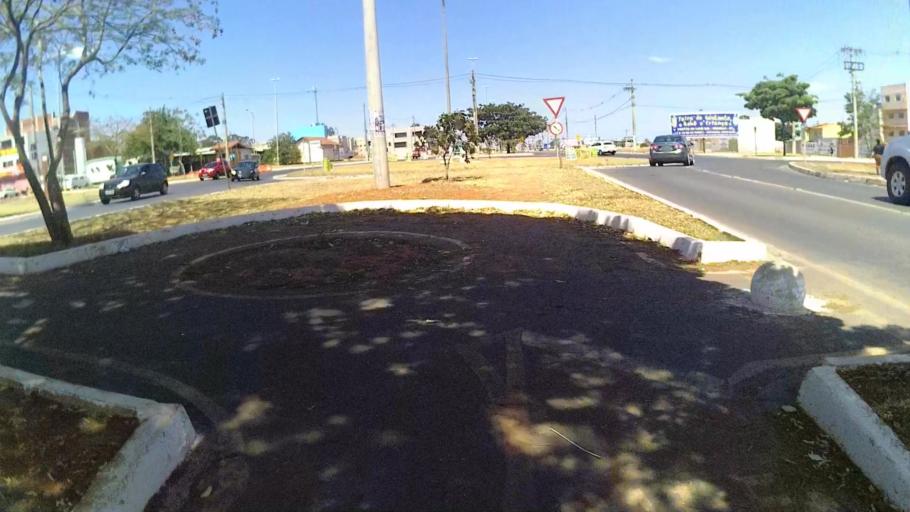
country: BR
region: Federal District
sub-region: Brasilia
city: Brasilia
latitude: -15.8988
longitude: -48.0473
